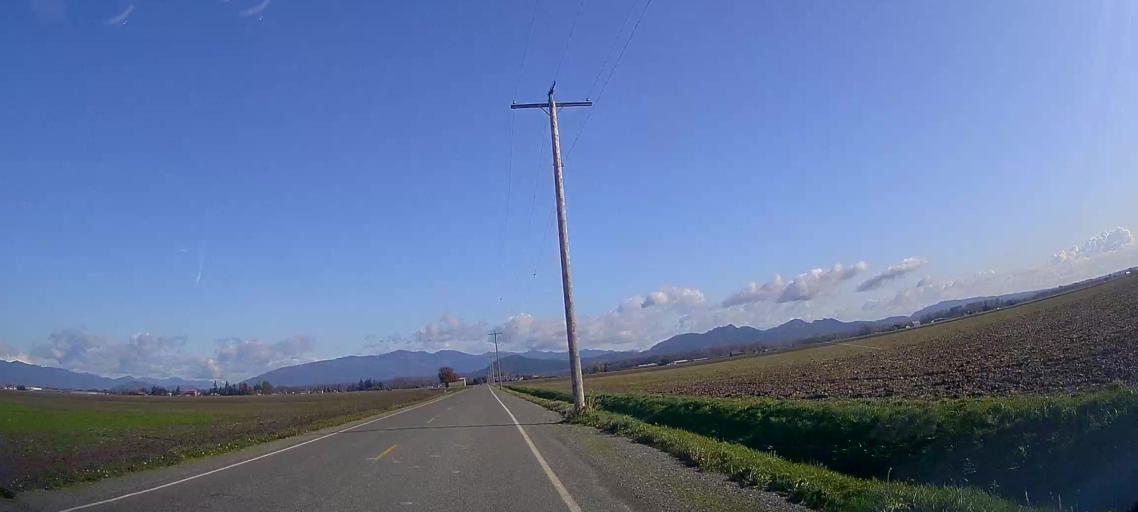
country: US
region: Washington
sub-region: Skagit County
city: Mount Vernon
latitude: 48.3991
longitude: -122.4174
